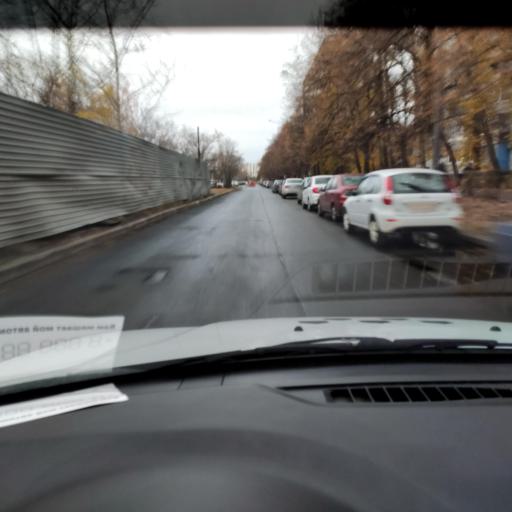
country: RU
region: Samara
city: Tol'yatti
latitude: 53.5321
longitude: 49.2834
